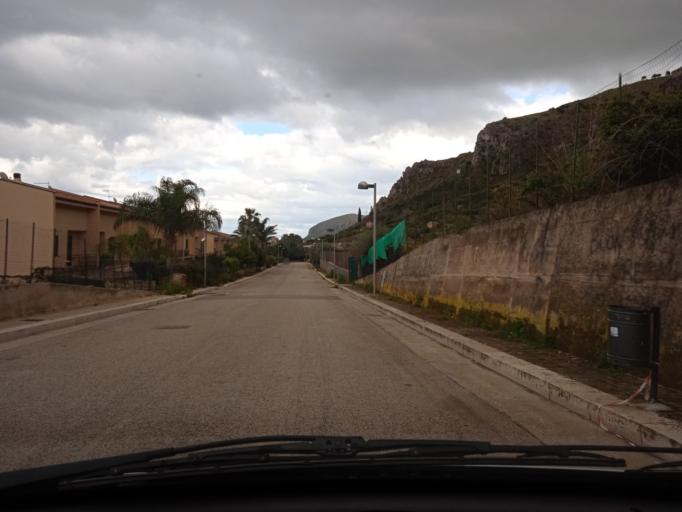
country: IT
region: Sicily
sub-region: Palermo
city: Villabate
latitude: 38.0722
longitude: 13.4384
